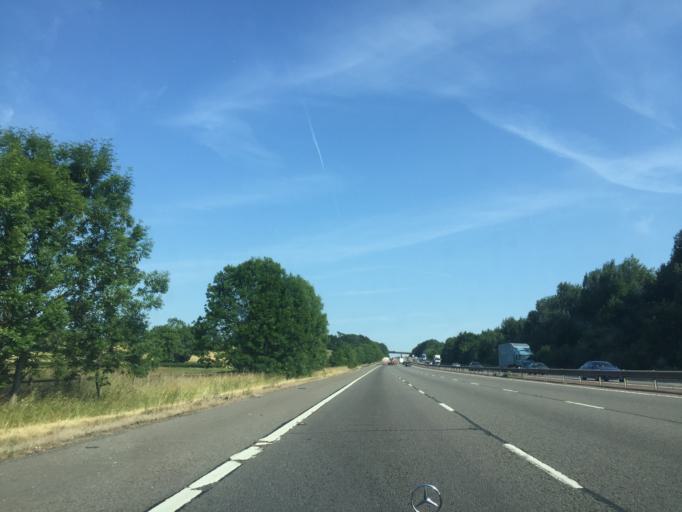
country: GB
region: England
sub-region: Oxfordshire
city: Hanwell
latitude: 52.0947
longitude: -1.3459
